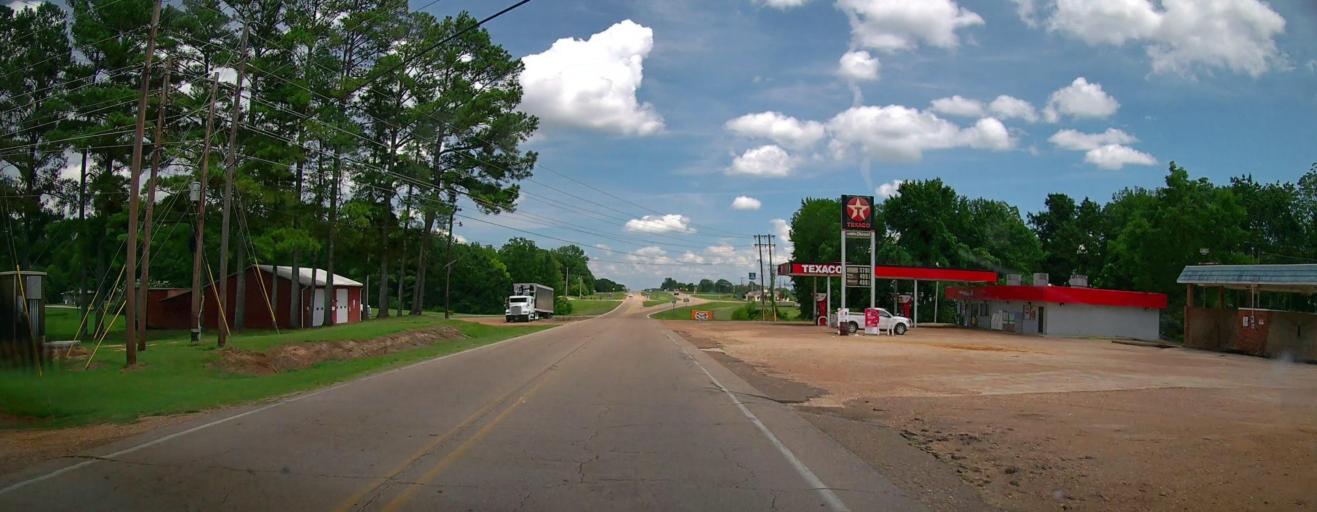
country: US
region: Mississippi
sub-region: Lee County
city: Shannon
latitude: 34.1198
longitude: -88.7087
